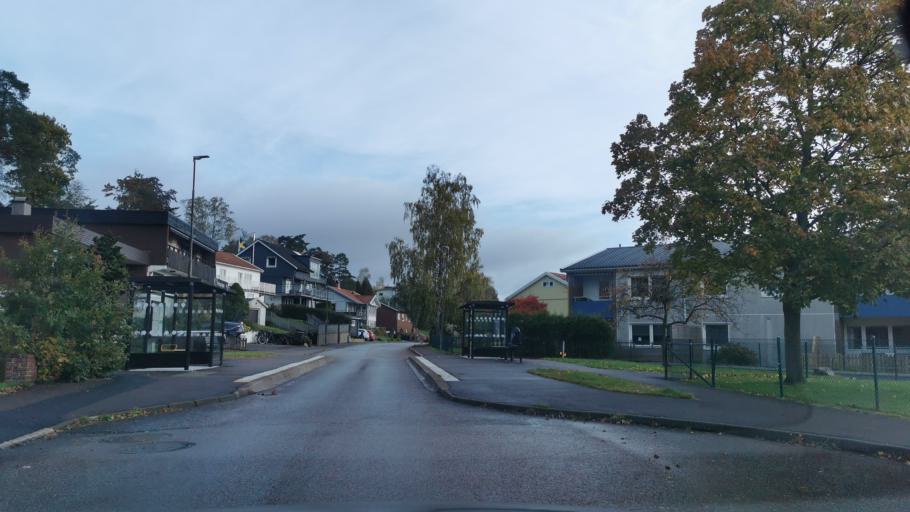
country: SE
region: Vaestra Goetaland
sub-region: Partille Kommun
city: Partille
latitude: 57.7234
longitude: 12.0732
